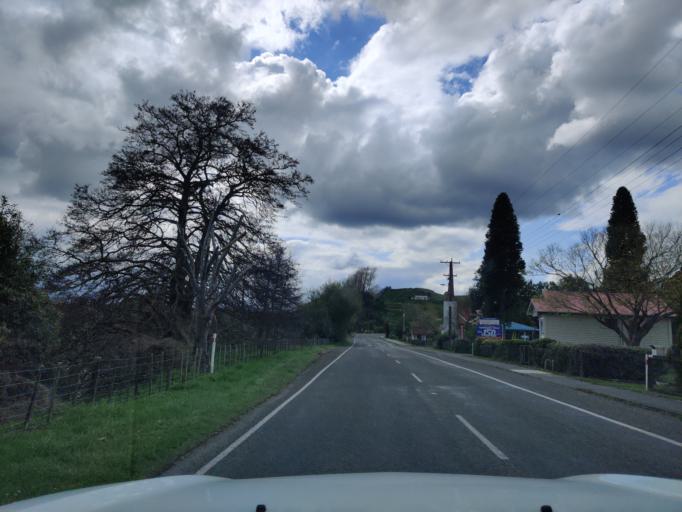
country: NZ
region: Manawatu-Wanganui
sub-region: Wanganui District
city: Wanganui
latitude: -39.8667
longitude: 175.1137
